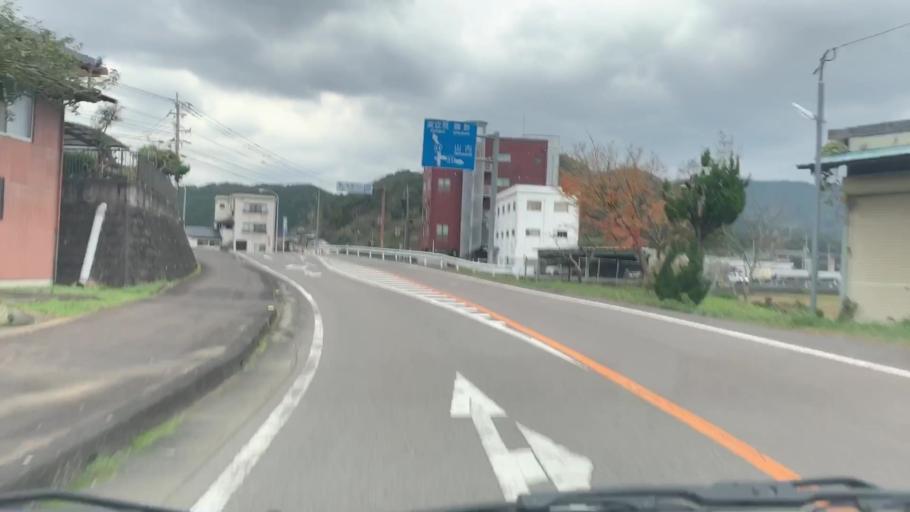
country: JP
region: Saga Prefecture
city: Ureshinomachi-shimojuku
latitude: 33.1383
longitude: 129.9801
